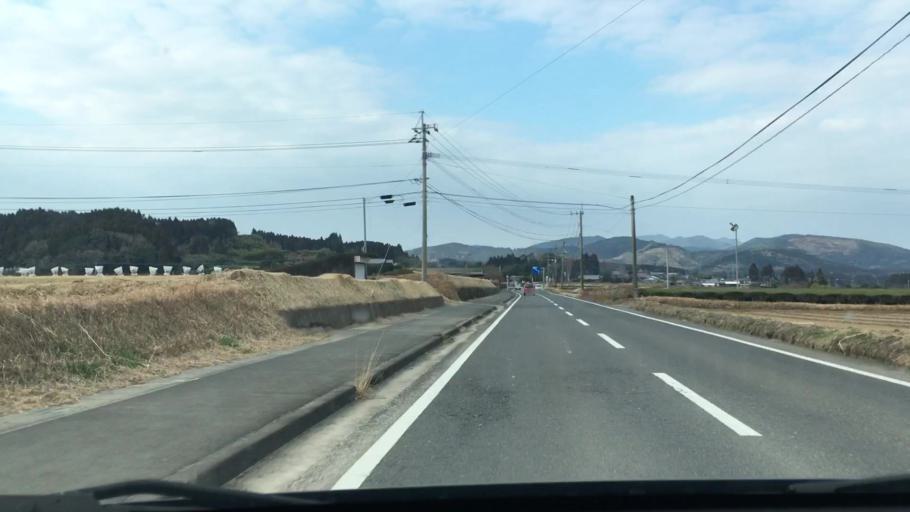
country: JP
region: Miyazaki
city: Kushima
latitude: 31.5167
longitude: 131.2391
